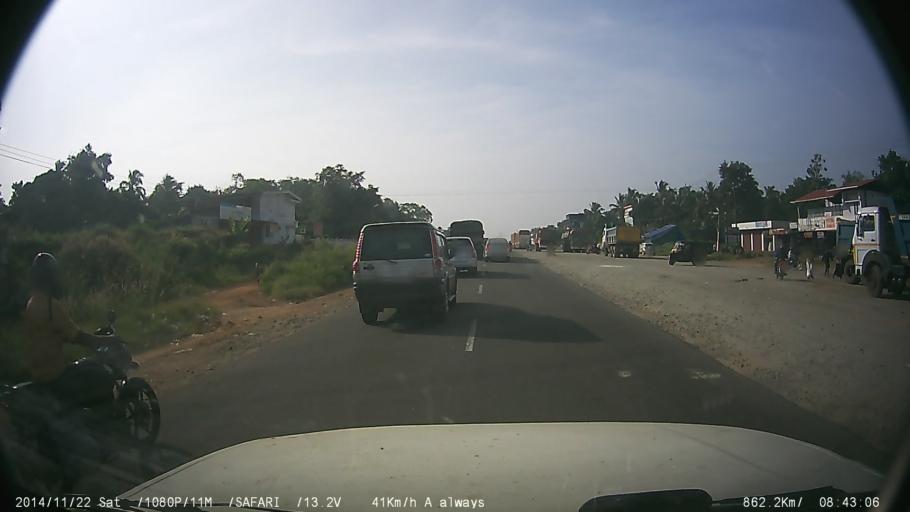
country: IN
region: Kerala
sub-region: Thrissur District
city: Trichur
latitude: 10.5179
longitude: 76.2587
